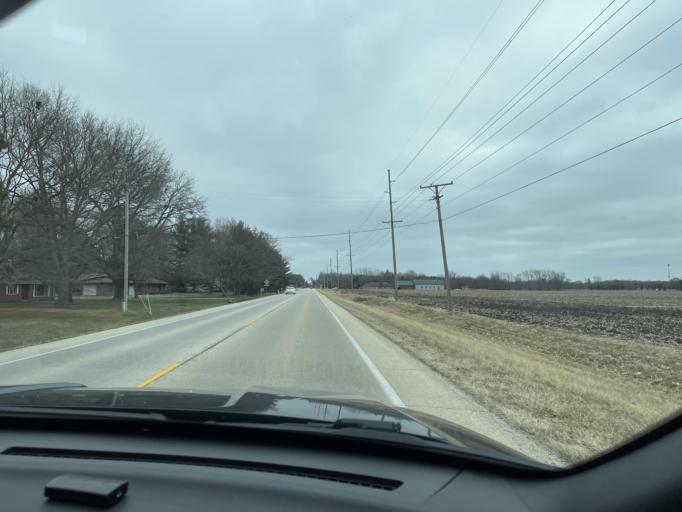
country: US
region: Illinois
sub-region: Sangamon County
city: Leland Grove
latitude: 39.7866
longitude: -89.7468
